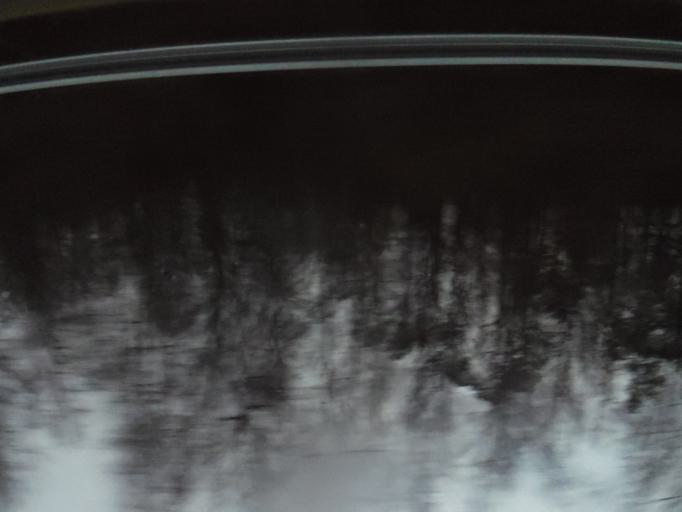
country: US
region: Alabama
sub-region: Cullman County
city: Cullman
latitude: 34.2526
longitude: -86.8903
